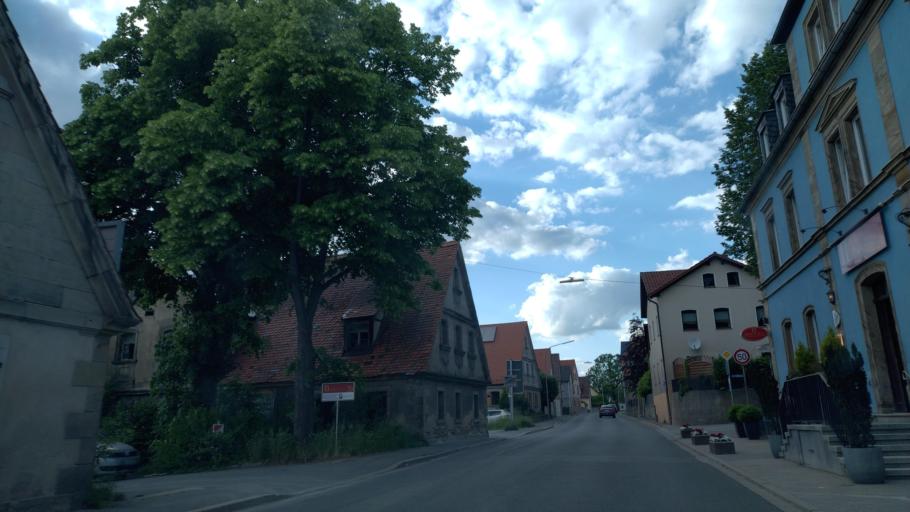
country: DE
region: Bavaria
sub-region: Upper Franconia
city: Bindlach
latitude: 49.9812
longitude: 11.6111
